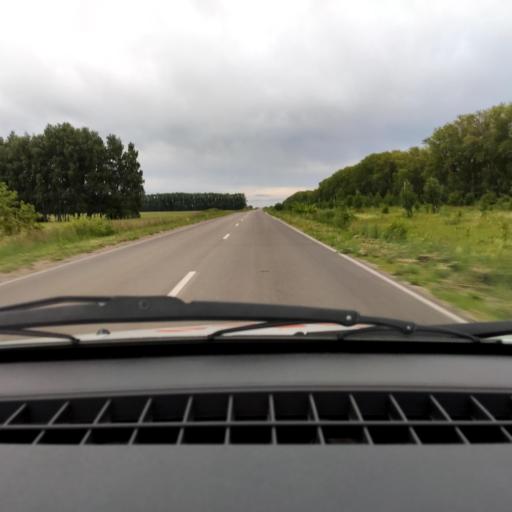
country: RU
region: Bashkortostan
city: Avdon
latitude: 54.5306
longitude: 55.7660
